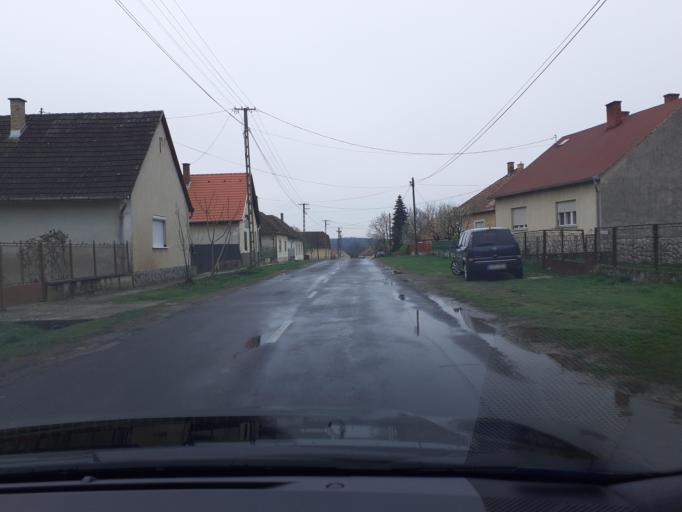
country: HU
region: Tolna
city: Hogyesz
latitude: 46.4217
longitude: 18.4545
